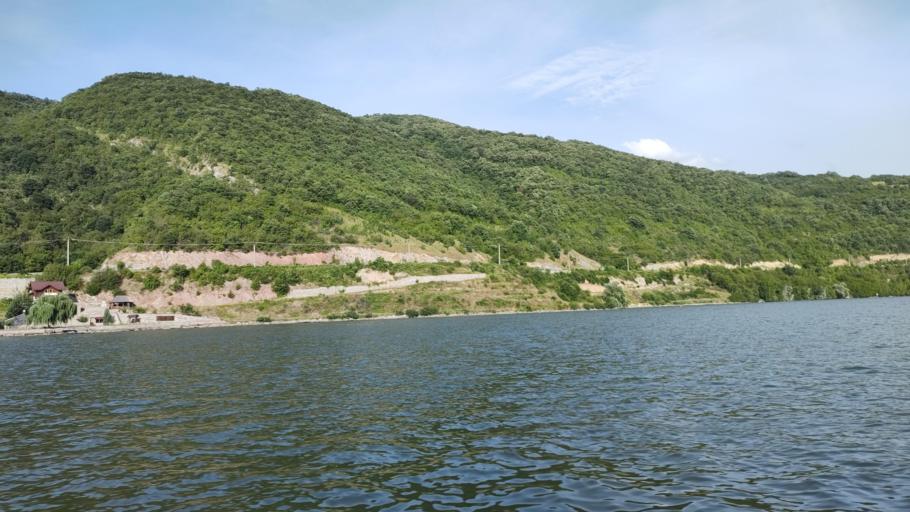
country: RO
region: Mehedinti
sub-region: Comuna Svinita
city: Svinita
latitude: 44.5192
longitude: 22.0750
